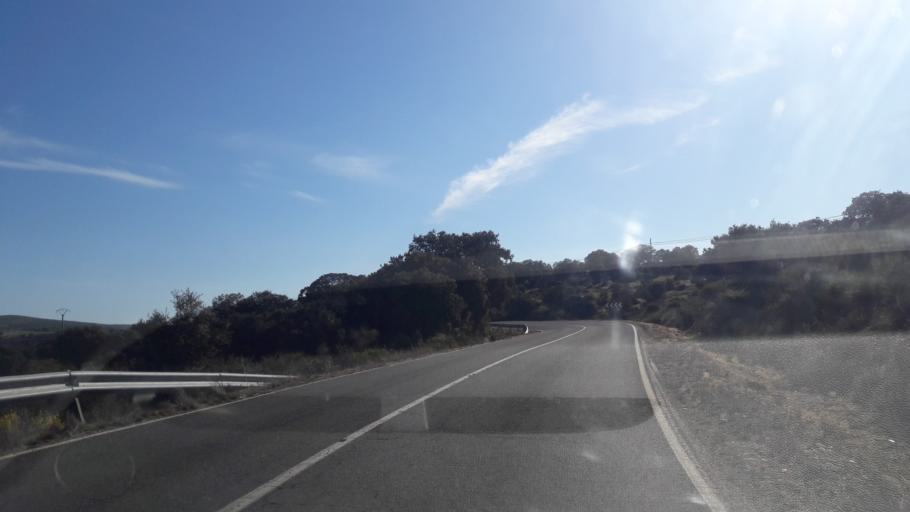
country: ES
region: Castille and Leon
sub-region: Provincia de Avila
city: Narrillos del Alamo
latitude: 40.5269
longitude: -5.4853
